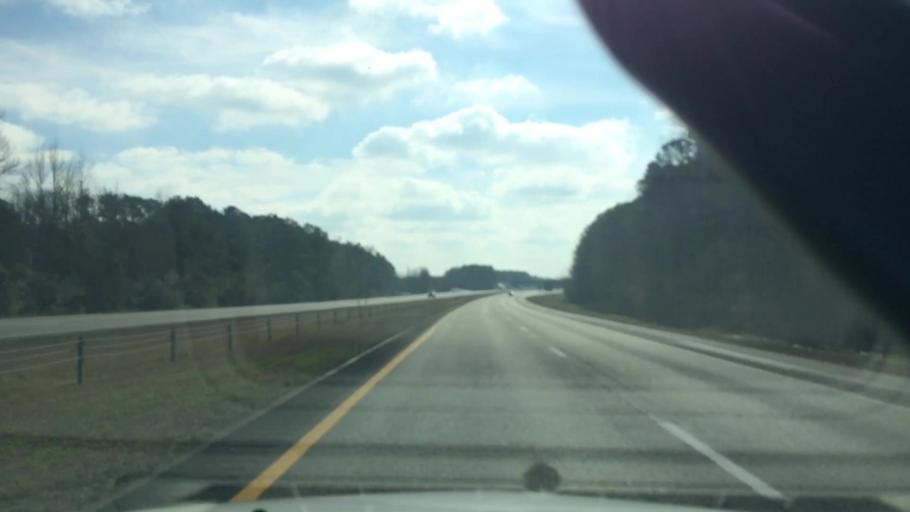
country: US
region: North Carolina
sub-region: Duplin County
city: Wallace
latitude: 34.6941
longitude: -77.9449
